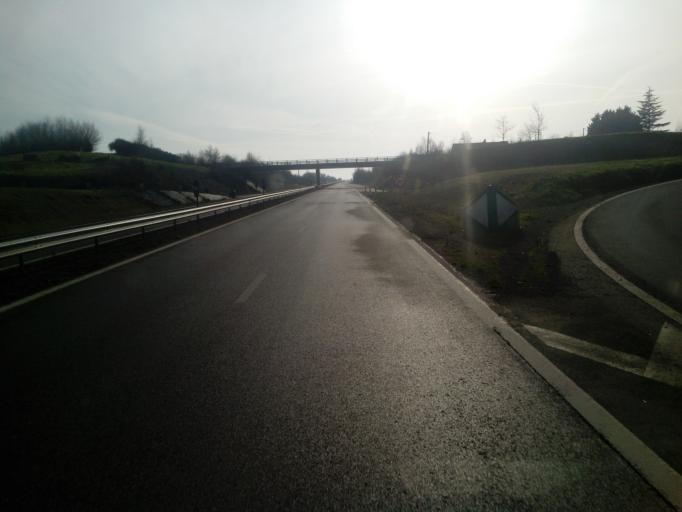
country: FR
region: Brittany
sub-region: Departement d'Ille-et-Vilaine
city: Betton
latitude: 48.1812
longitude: -1.6247
